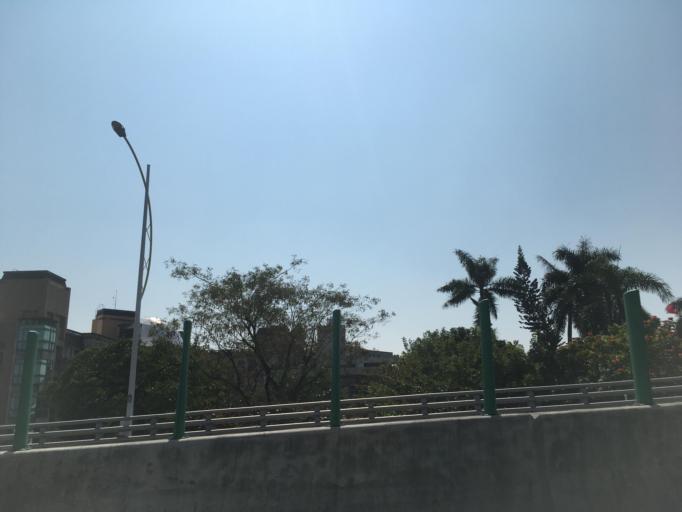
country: TW
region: Taiwan
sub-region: Chiayi
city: Jiayi Shi
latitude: 23.5495
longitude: 120.4311
